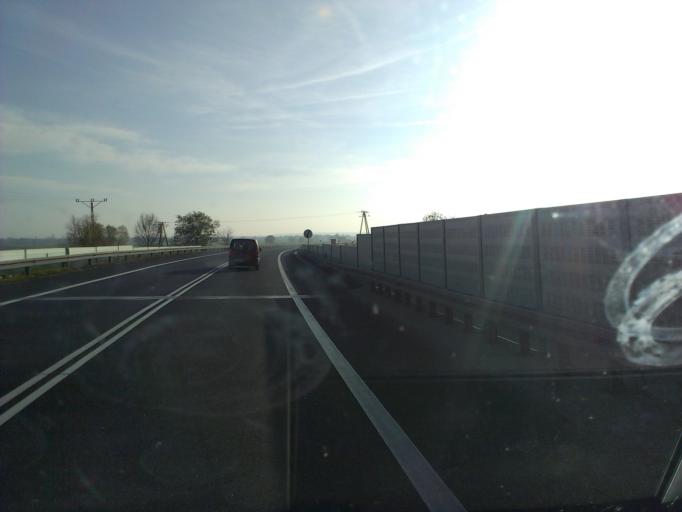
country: PL
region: Lower Silesian Voivodeship
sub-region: Legnica
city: Legnica
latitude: 51.2491
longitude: 16.1496
